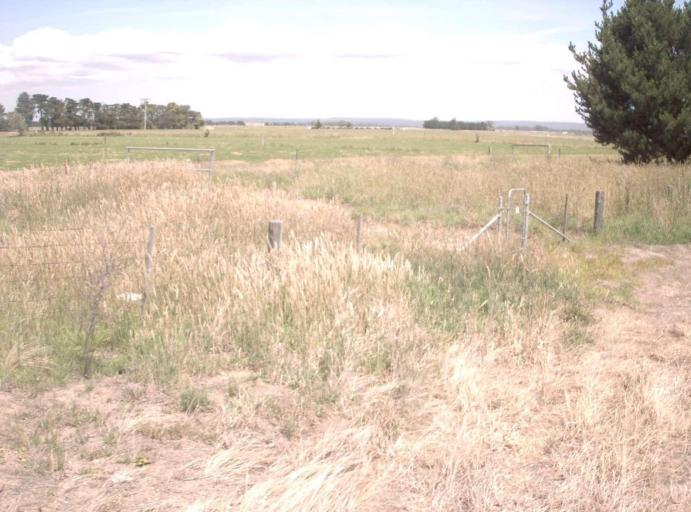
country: AU
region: Victoria
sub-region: Wellington
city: Heyfield
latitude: -38.0718
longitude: 146.8705
